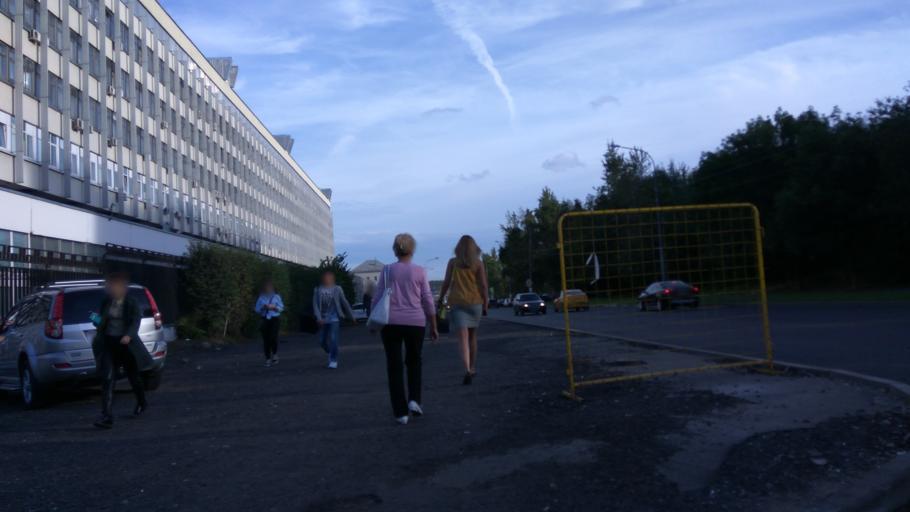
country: RU
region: Moscow
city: Tsaritsyno
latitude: 55.6243
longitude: 37.6673
